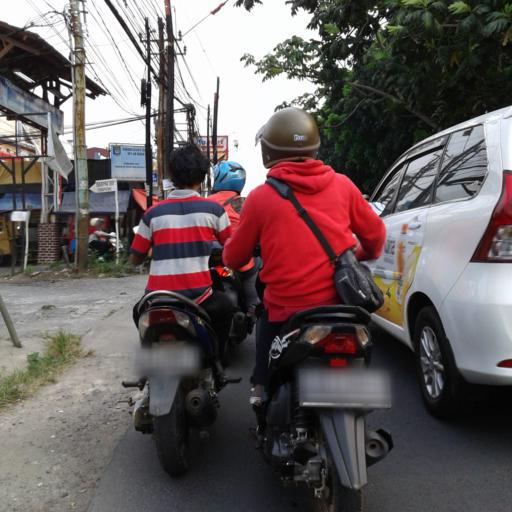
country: ID
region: West Java
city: Sawangan
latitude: -6.3853
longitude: 106.7687
